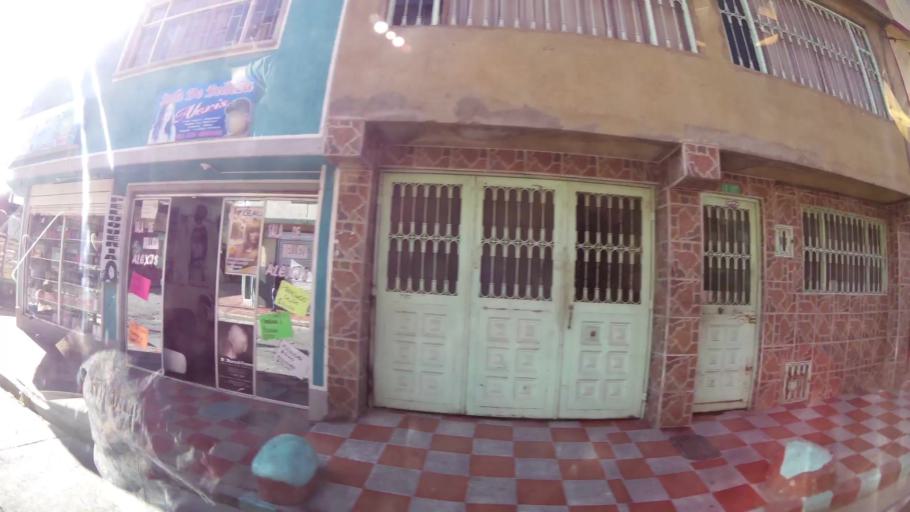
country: CO
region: Cundinamarca
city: Soacha
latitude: 4.5615
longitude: -74.1461
